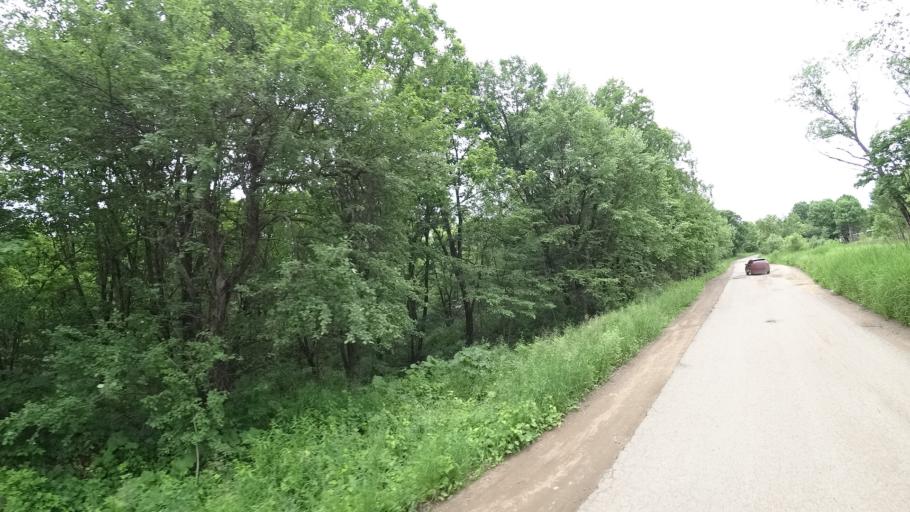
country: RU
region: Primorskiy
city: Novosysoyevka
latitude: 44.2016
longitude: 133.3198
